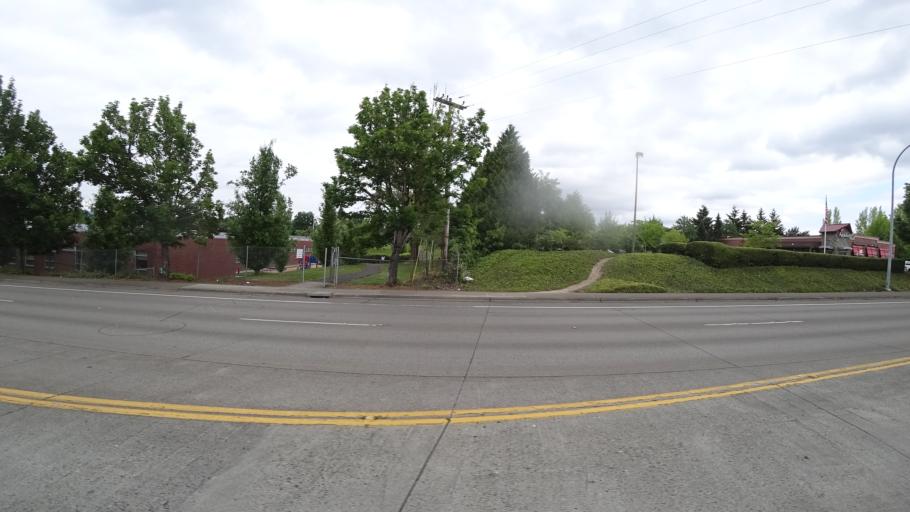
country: US
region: Oregon
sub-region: Washington County
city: Rockcreek
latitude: 45.5292
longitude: -122.8674
